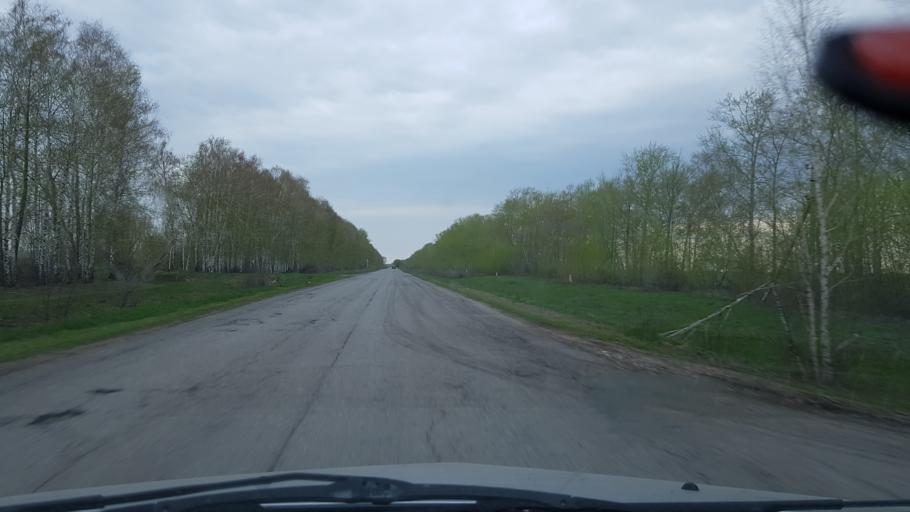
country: RU
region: Samara
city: Podstepki
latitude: 53.6636
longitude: 49.1888
